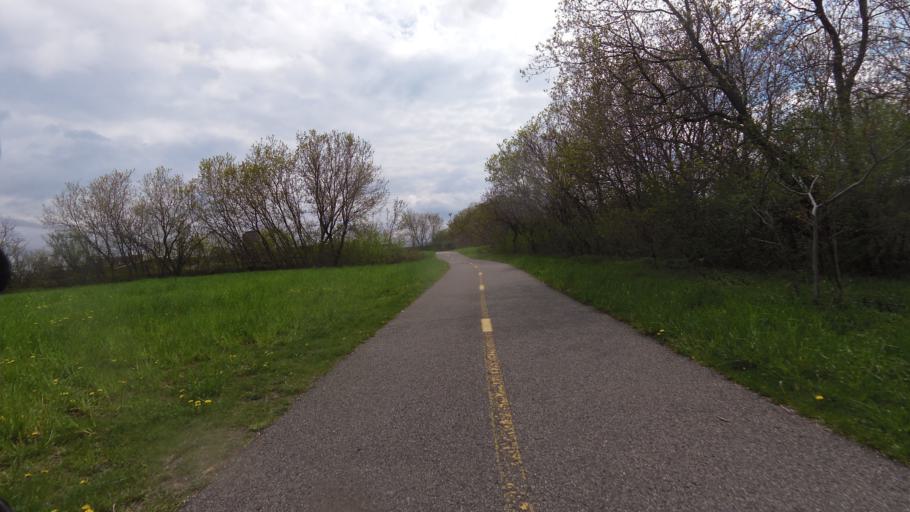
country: CA
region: Ontario
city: Ottawa
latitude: 45.4384
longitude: -75.7247
